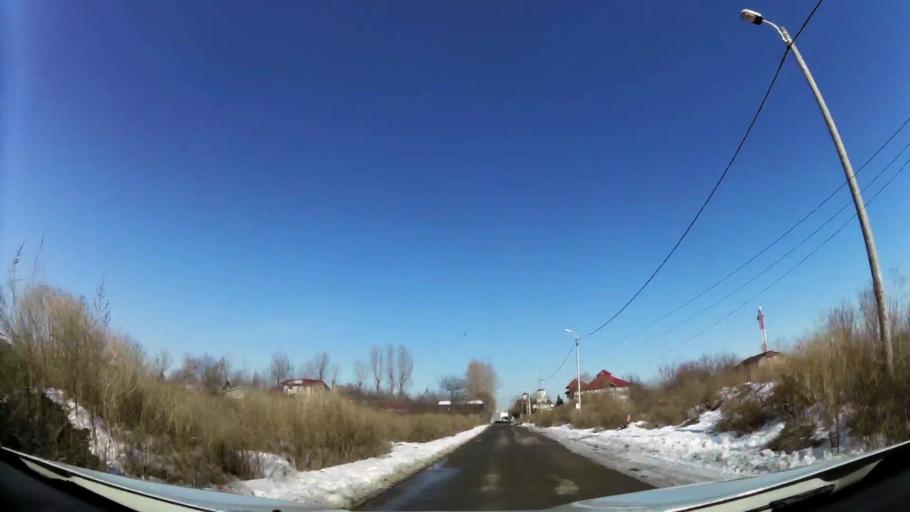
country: RO
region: Ilfov
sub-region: Comuna Magurele
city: Magurele
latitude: 44.3871
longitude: 26.0528
